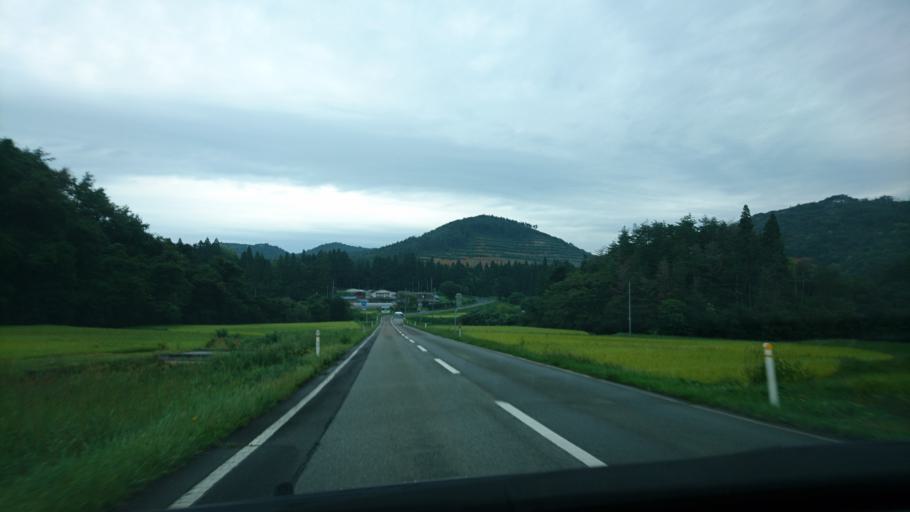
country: JP
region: Iwate
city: Mizusawa
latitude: 39.0251
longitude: 141.2026
